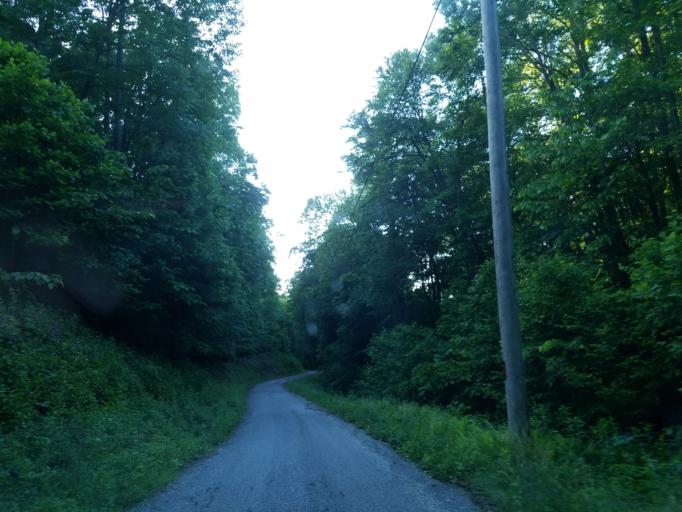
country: US
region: Georgia
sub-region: Lumpkin County
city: Dahlonega
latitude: 34.7046
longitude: -84.0124
